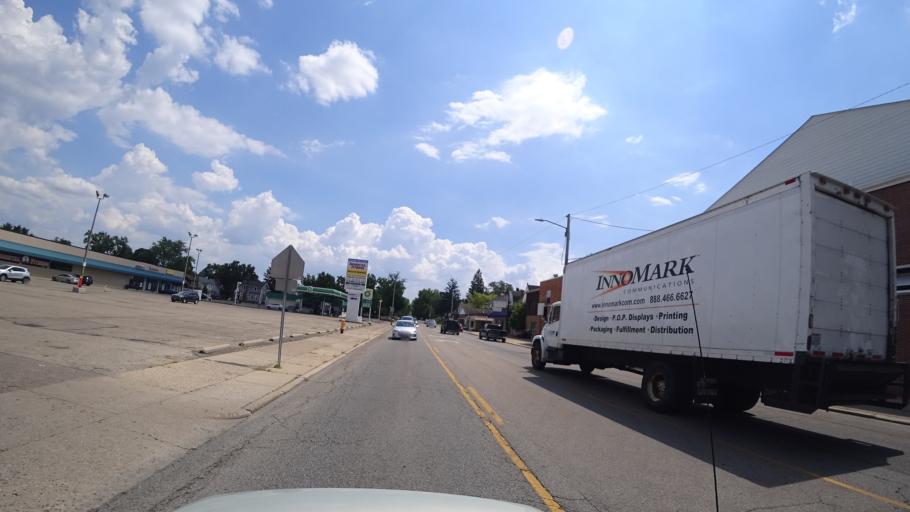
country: US
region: Ohio
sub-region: Butler County
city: Hamilton
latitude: 39.4126
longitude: -84.5805
